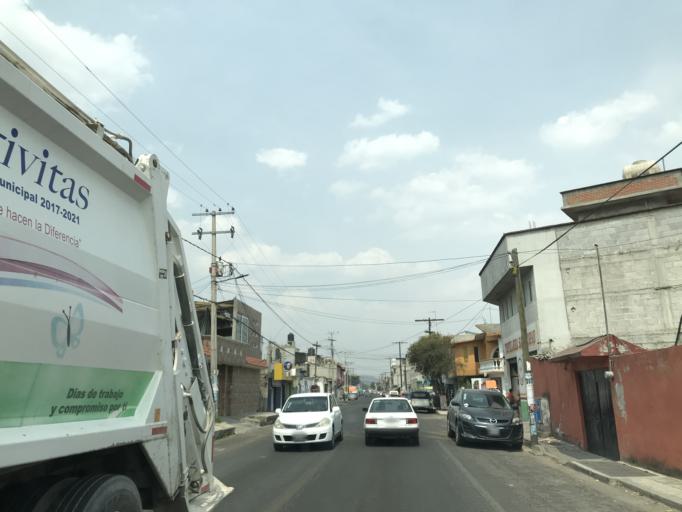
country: MX
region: Tlaxcala
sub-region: Ixtacuixtla de Mariano Matamoros
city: Santa Justina Ecatepec
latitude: 19.3181
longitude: -98.3159
